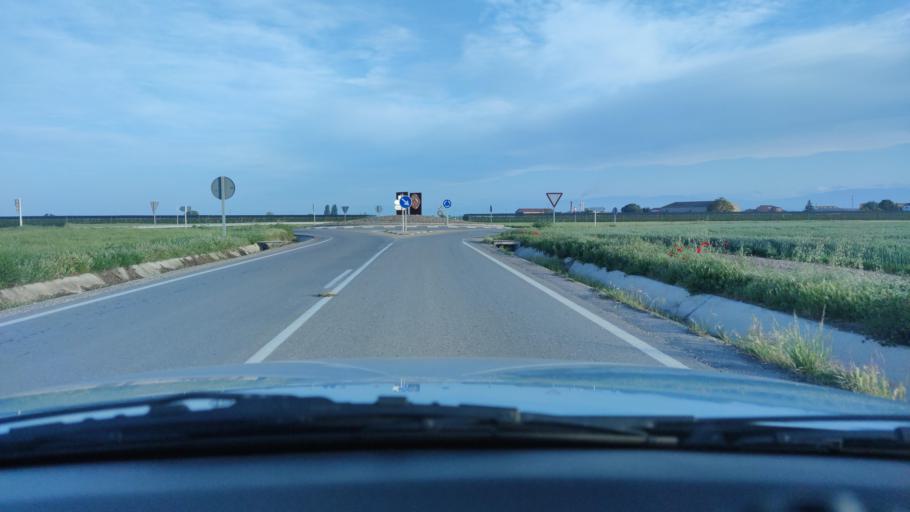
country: ES
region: Catalonia
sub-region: Provincia de Lleida
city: Ivars d'Urgell
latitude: 41.6750
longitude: 0.9841
